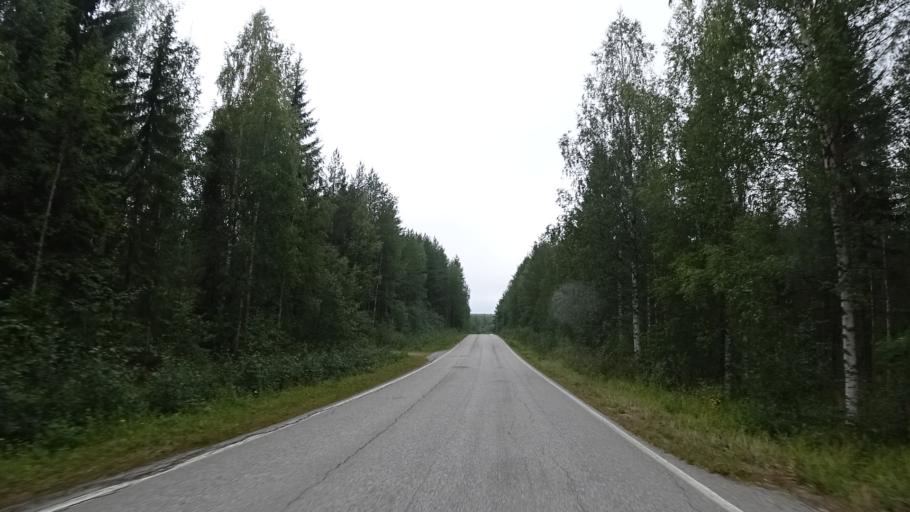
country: FI
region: North Karelia
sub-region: Pielisen Karjala
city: Lieksa
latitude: 63.3231
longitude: 30.2202
